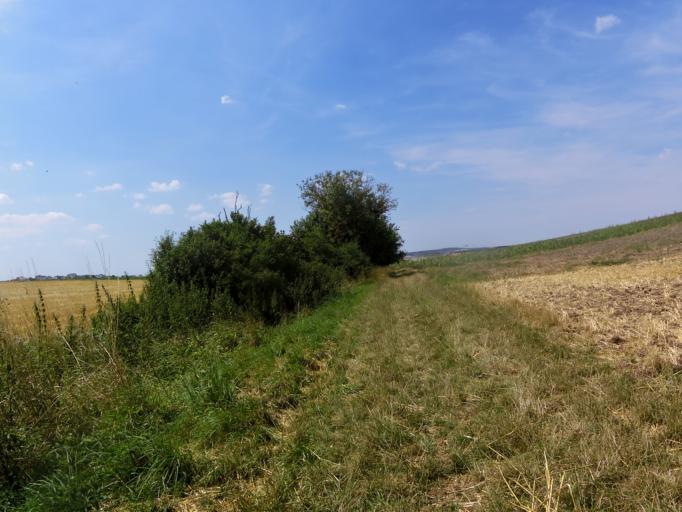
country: DE
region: Bavaria
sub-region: Regierungsbezirk Unterfranken
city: Estenfeld
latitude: 49.8069
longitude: 10.0105
